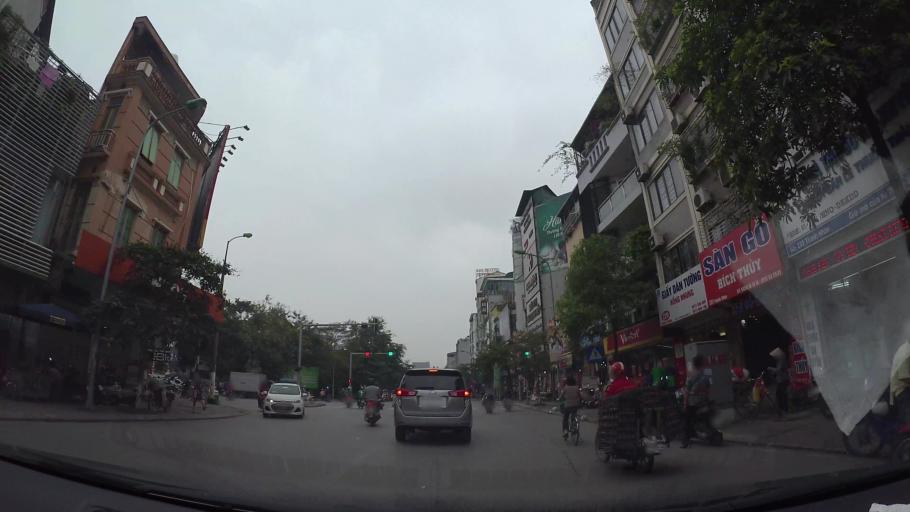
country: VN
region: Ha Noi
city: Hai BaTrung
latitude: 21.0027
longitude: 105.8543
